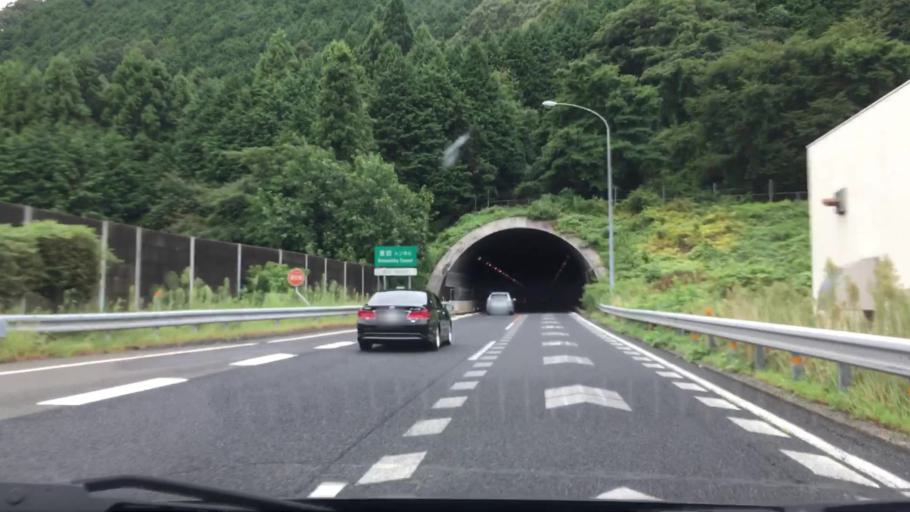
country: JP
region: Hyogo
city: Yamazakicho-nakabirose
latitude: 35.0371
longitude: 134.4191
